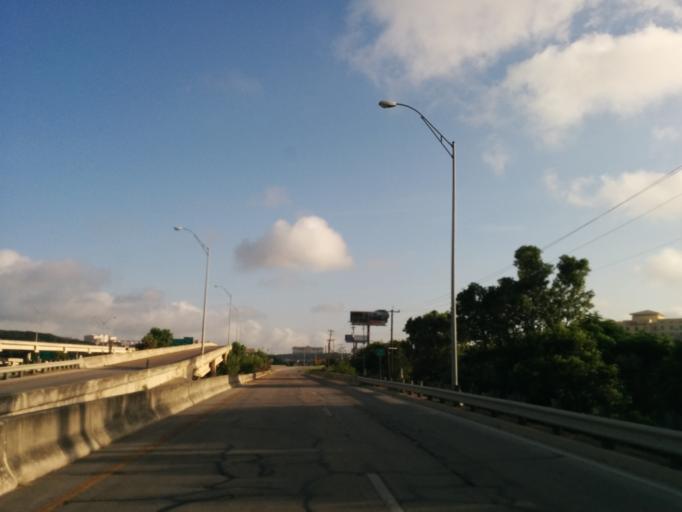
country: US
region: Texas
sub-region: Bexar County
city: Shavano Park
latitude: 29.5994
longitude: -98.5994
